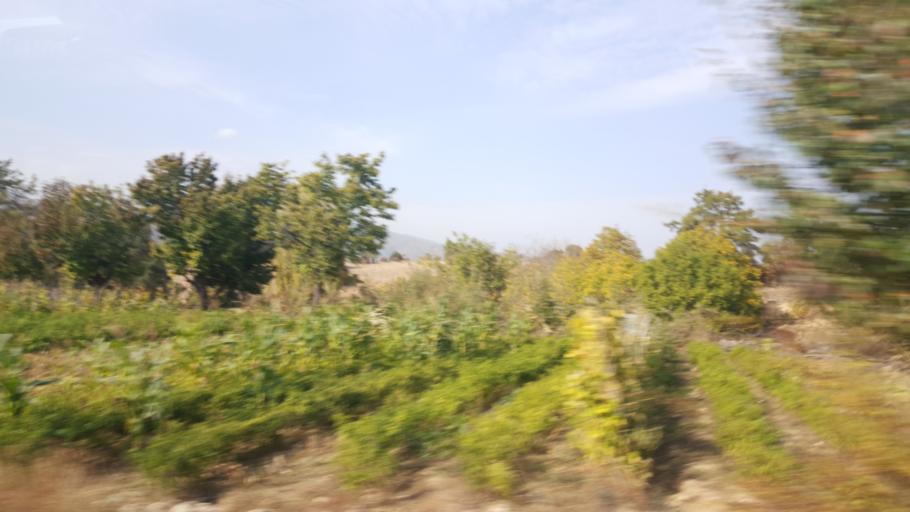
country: TR
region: Eskisehir
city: Mihaliccik
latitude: 39.9818
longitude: 31.3762
